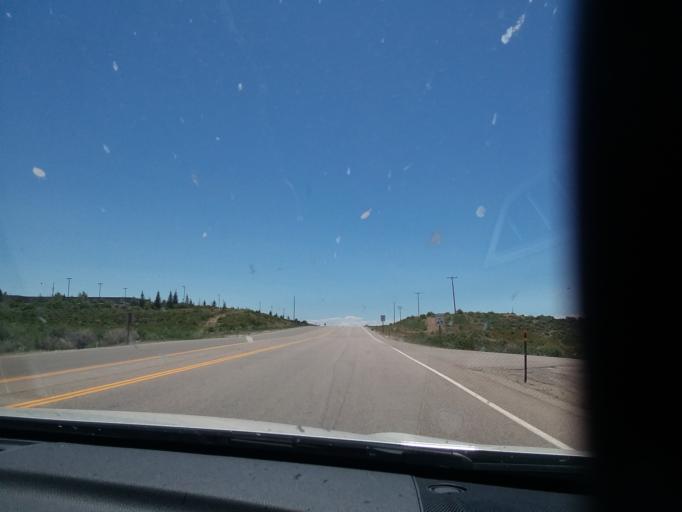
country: US
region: Wyoming
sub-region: Sweetwater County
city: North Rock Springs
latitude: 41.6307
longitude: -109.2317
